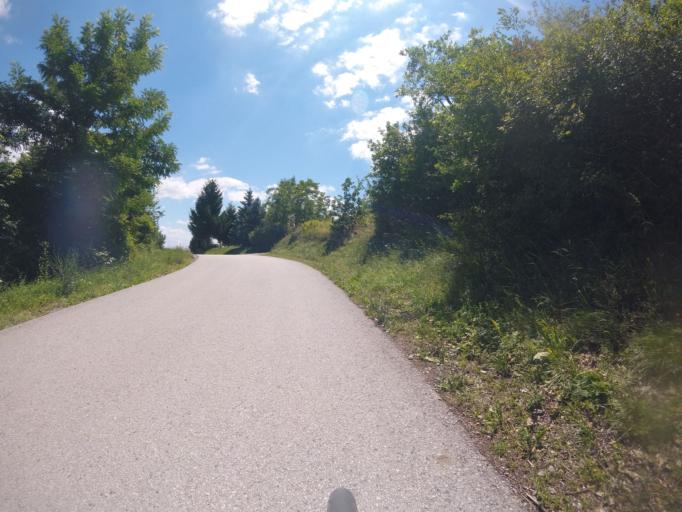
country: HR
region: Karlovacka
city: Ozalj
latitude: 45.6821
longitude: 15.4101
